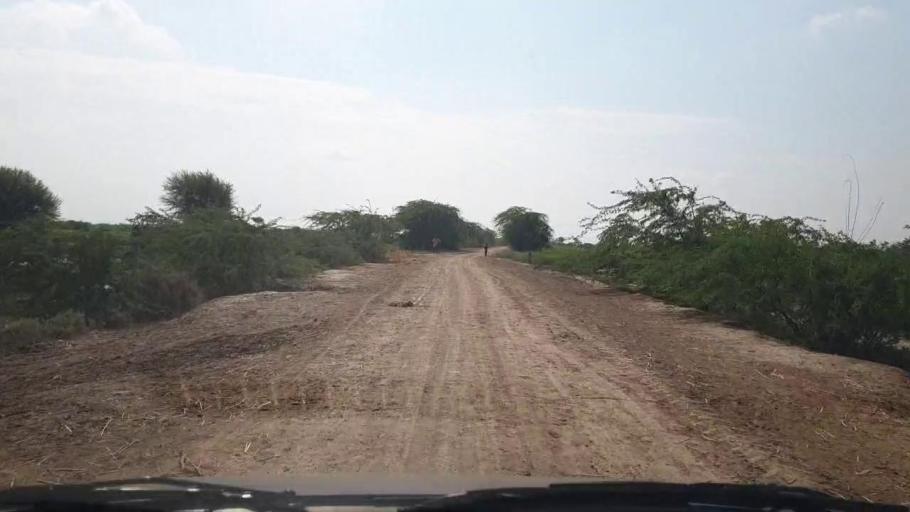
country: PK
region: Sindh
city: Badin
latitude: 24.4869
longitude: 68.6120
